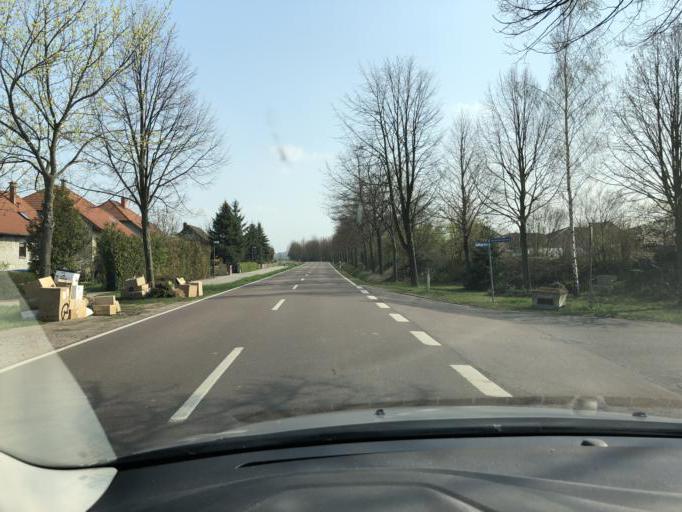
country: DE
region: Saxony-Anhalt
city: Hohenthurm
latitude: 51.4975
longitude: 12.1007
